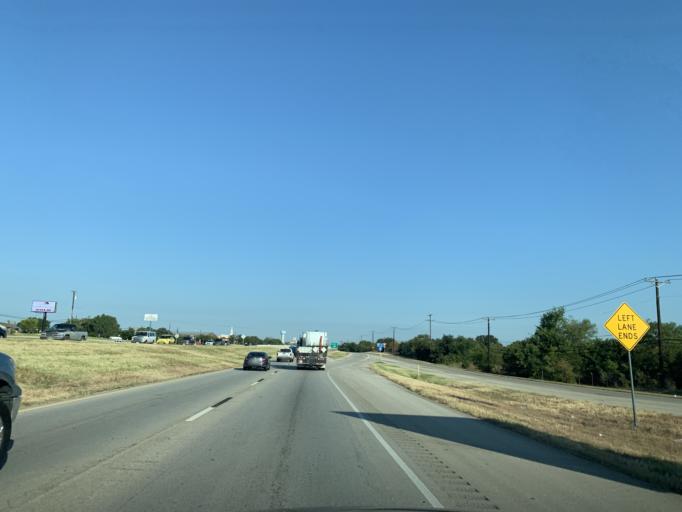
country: US
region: Texas
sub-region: Tarrant County
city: Lakeside
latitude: 32.8230
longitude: -97.4715
